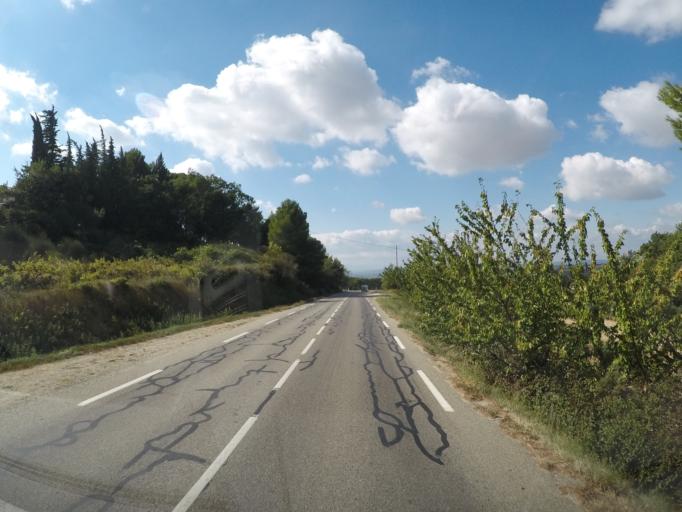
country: FR
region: Provence-Alpes-Cote d'Azur
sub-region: Departement du Vaucluse
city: Visan
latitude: 44.2745
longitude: 5.0019
